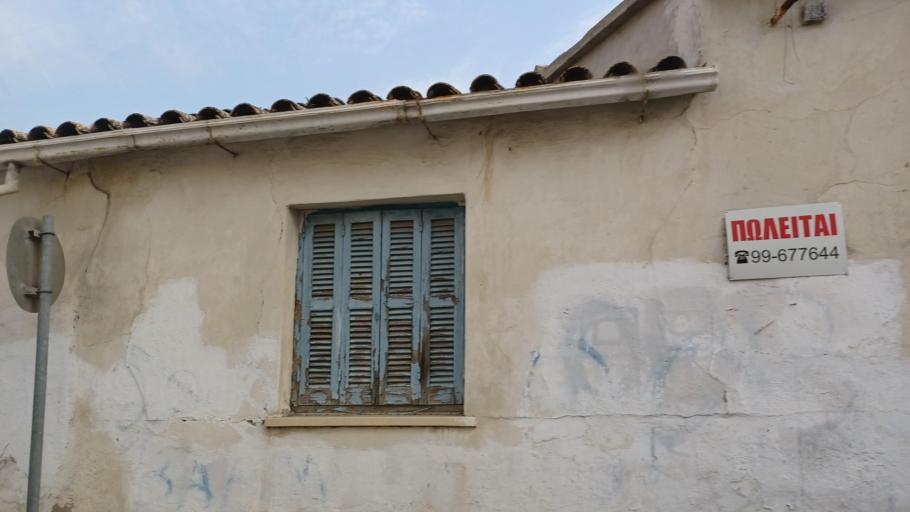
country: CY
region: Larnaka
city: Athienou
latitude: 35.0612
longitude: 33.5414
